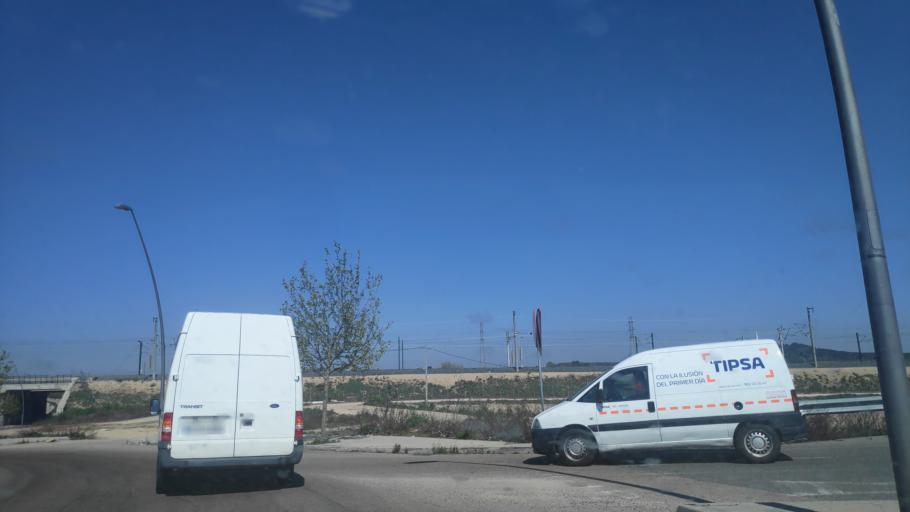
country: ES
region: Madrid
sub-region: Provincia de Madrid
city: Pinto
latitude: 40.2895
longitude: -3.6804
